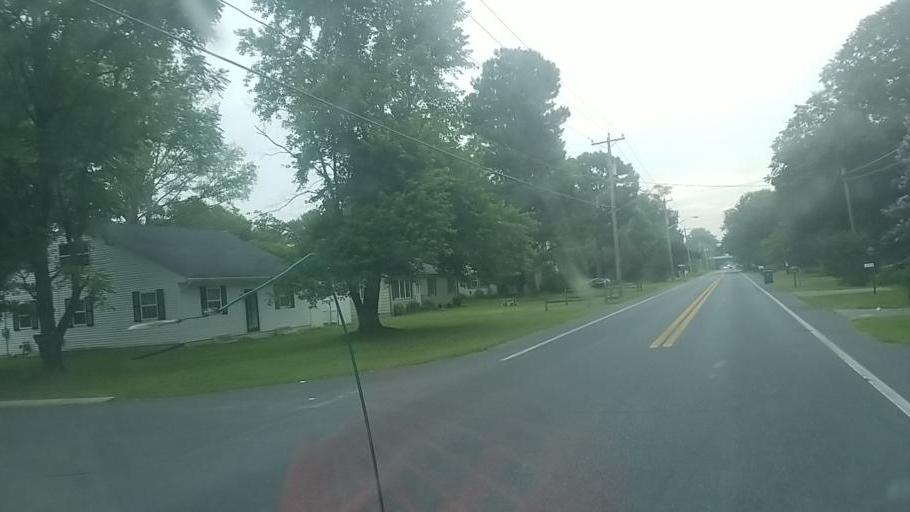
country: US
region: Maryland
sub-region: Wicomico County
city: Salisbury
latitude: 38.3739
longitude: -75.5437
